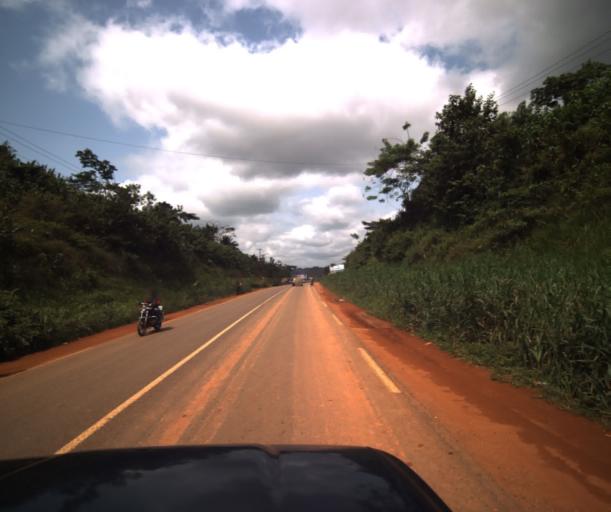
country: CM
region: Centre
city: Yaounde
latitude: 3.7956
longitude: 11.4963
